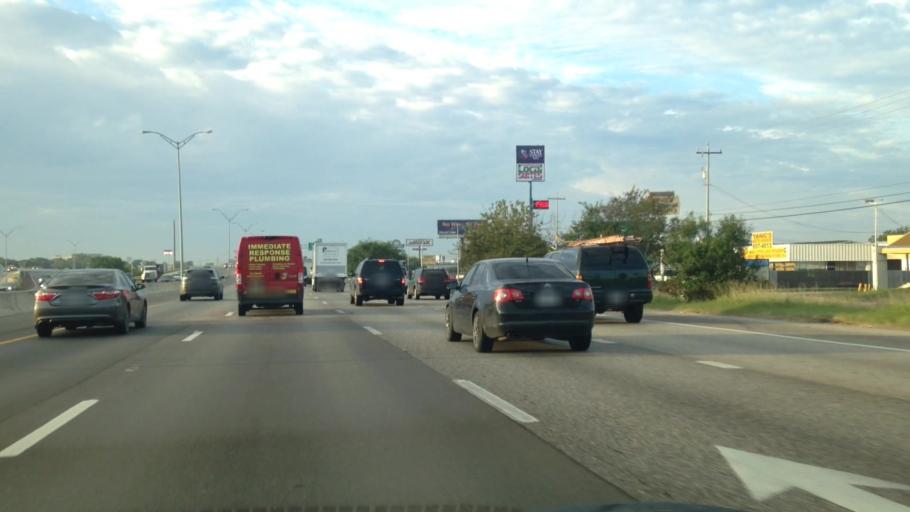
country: US
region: Texas
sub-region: Bexar County
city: Windcrest
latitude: 29.5271
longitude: -98.3934
